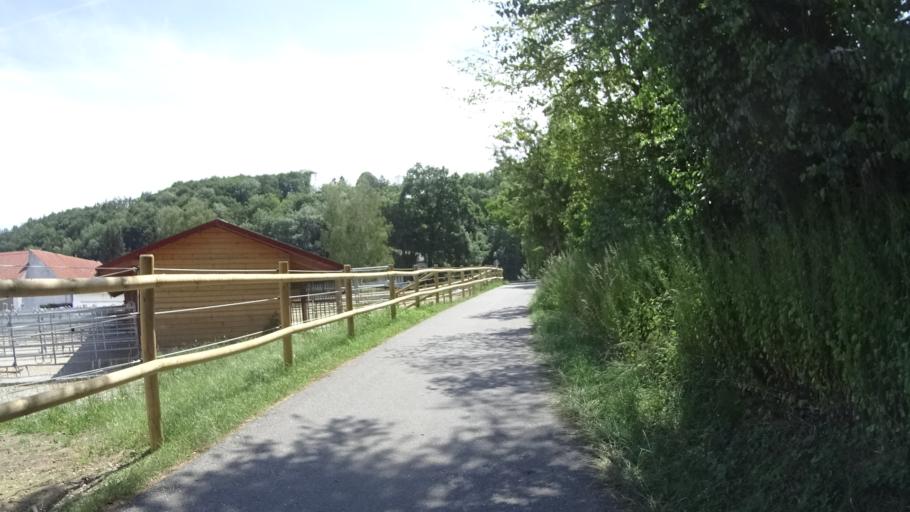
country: DE
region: Bavaria
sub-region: Lower Bavaria
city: Bad Abbach
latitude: 48.9255
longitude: 12.0147
